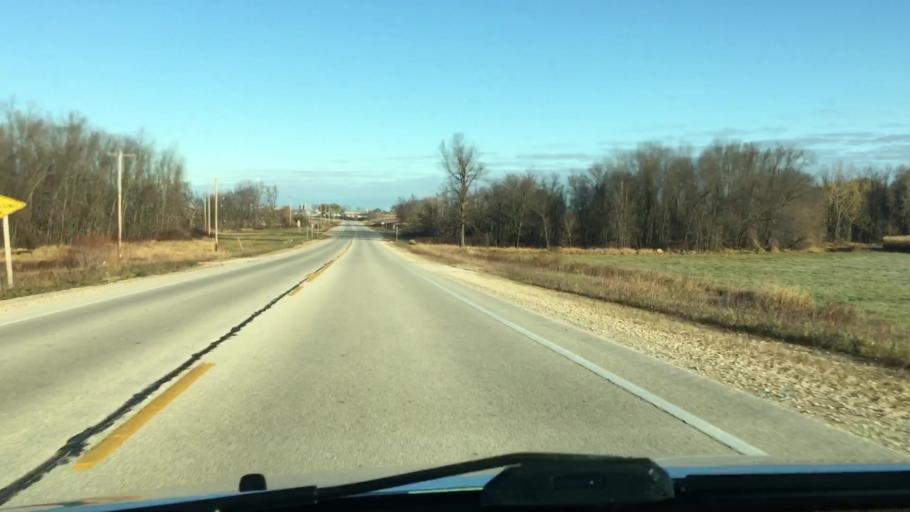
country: US
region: Wisconsin
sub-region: Dodge County
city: Lomira
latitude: 43.5560
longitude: -88.4442
